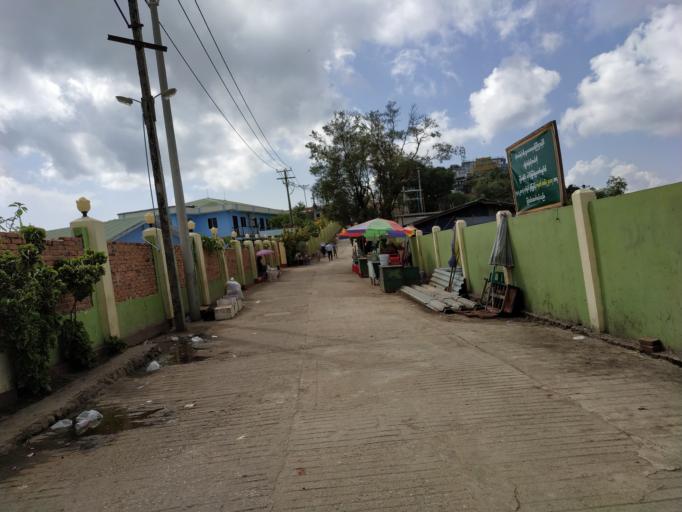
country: MM
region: Mon
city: Kyaikto
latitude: 17.4777
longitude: 97.1010
